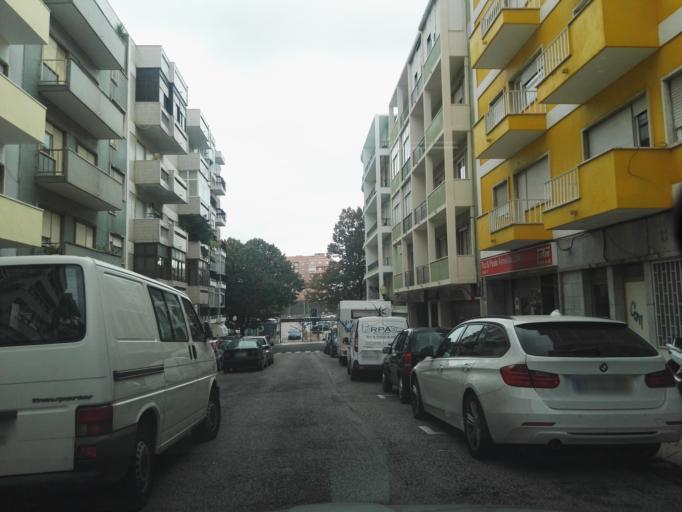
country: PT
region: Lisbon
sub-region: Lisbon
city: Lisbon
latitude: 38.7433
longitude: -9.1427
